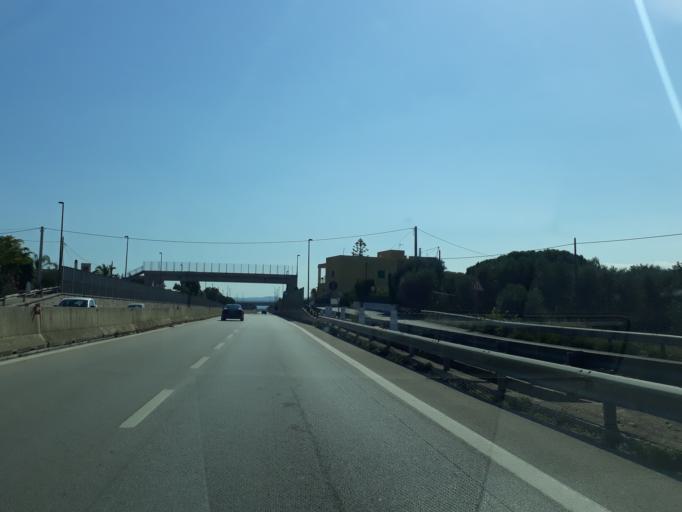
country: IT
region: Apulia
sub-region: Provincia di Brindisi
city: Fasano
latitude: 40.8853
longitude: 17.3356
